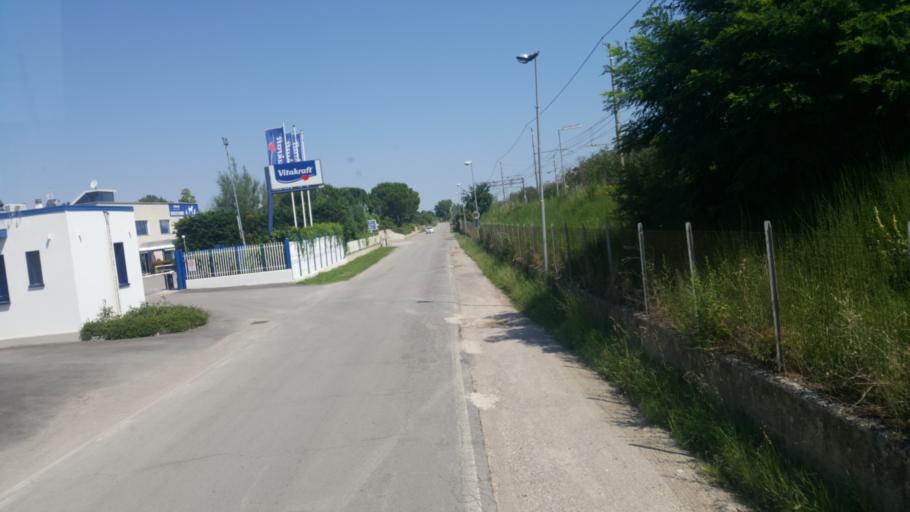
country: IT
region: Umbria
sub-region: Provincia di Perugia
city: Castiglione del Lago
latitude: 43.1260
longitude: 12.0308
